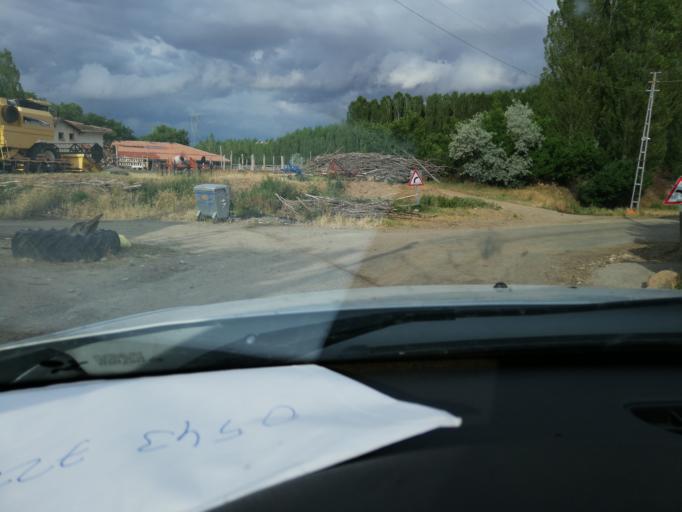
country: TR
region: Kirsehir
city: Kirsehir
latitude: 39.0288
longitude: 34.1291
